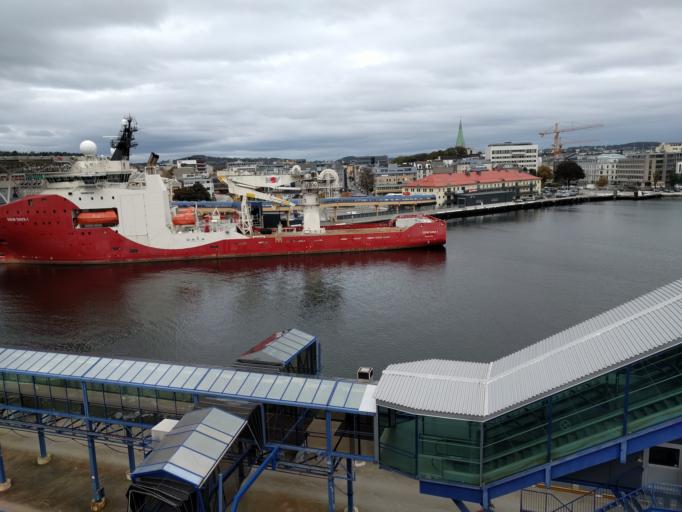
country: NO
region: Vest-Agder
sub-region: Kristiansand
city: Kristiansand
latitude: 58.1432
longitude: 7.9858
